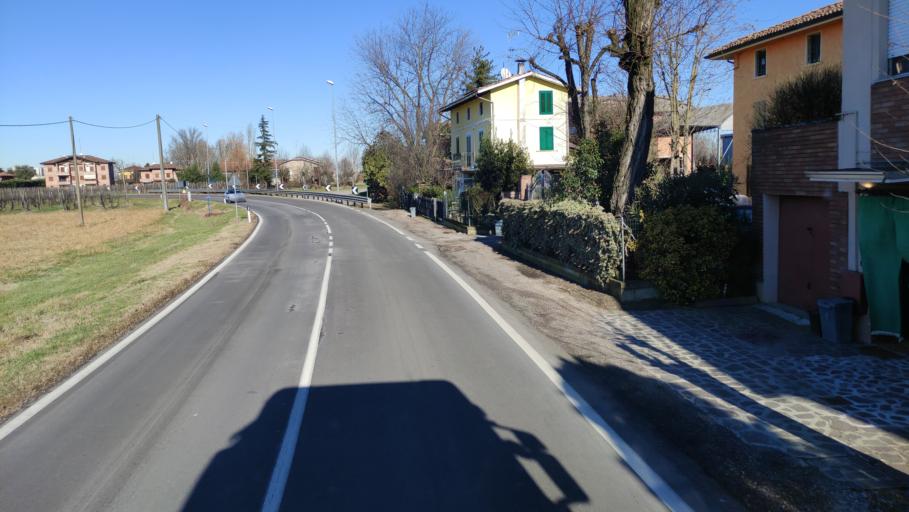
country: IT
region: Emilia-Romagna
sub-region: Provincia di Reggio Emilia
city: Rio Saliceto
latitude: 44.8061
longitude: 10.7835
